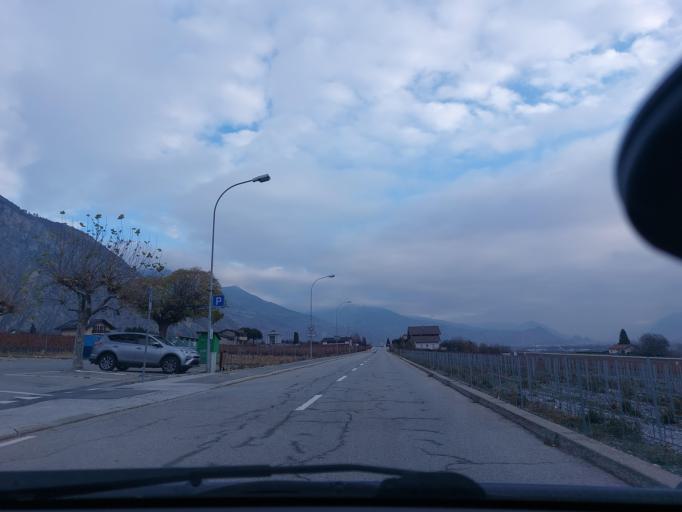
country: CH
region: Valais
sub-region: Conthey District
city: Chamoson
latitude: 46.1931
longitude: 7.2382
